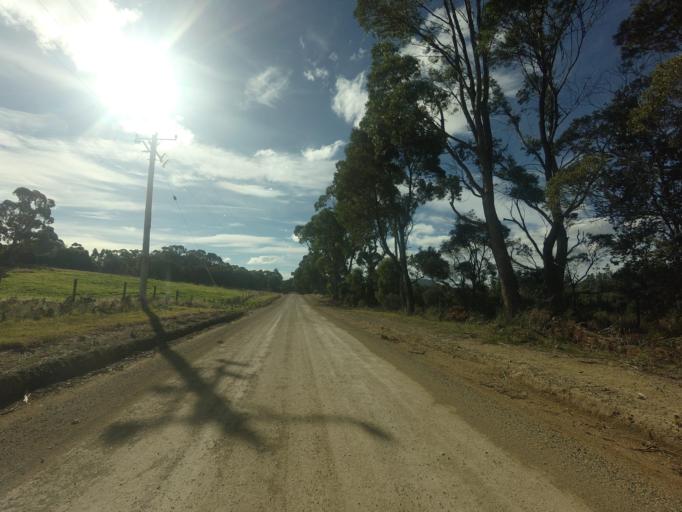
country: AU
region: Tasmania
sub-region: Clarence
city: Sandford
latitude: -43.1651
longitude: 147.7682
